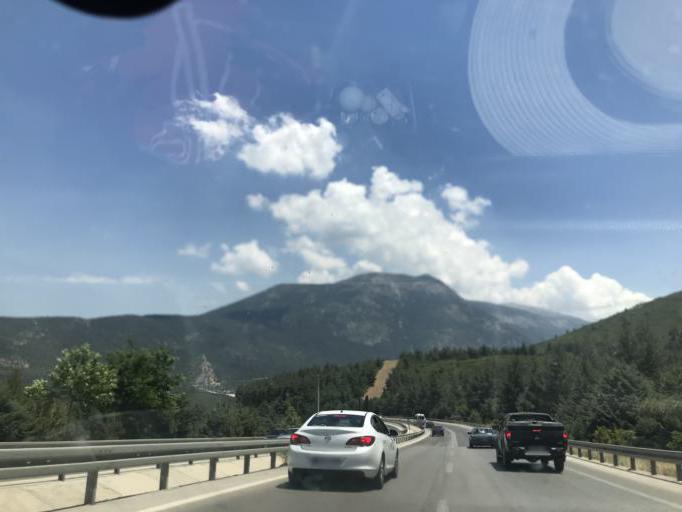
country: TR
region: Denizli
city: Honaz
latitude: 37.7308
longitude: 29.1847
